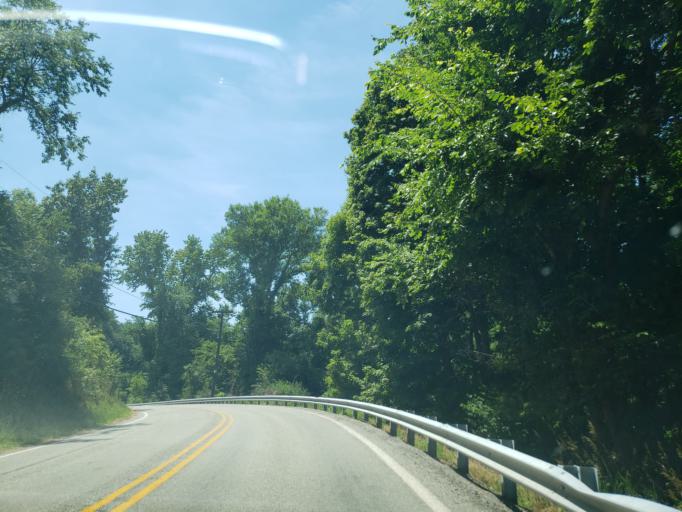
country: US
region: Pennsylvania
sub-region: Allegheny County
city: Emsworth
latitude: 40.5317
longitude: -80.1053
